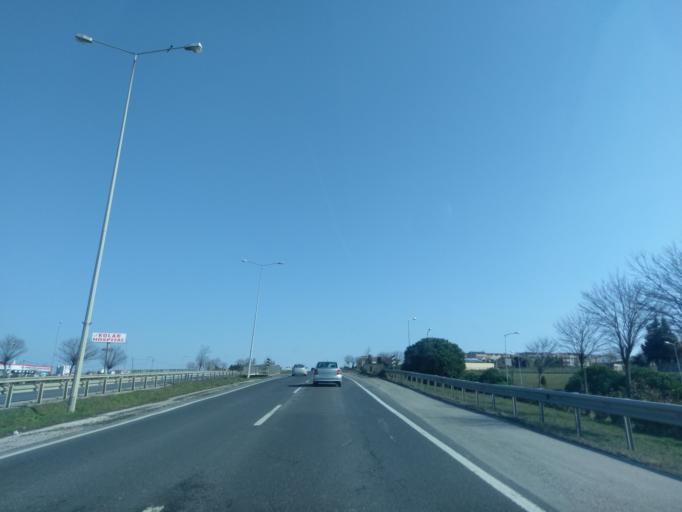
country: TR
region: Istanbul
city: Silivri
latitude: 41.0733
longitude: 28.2651
